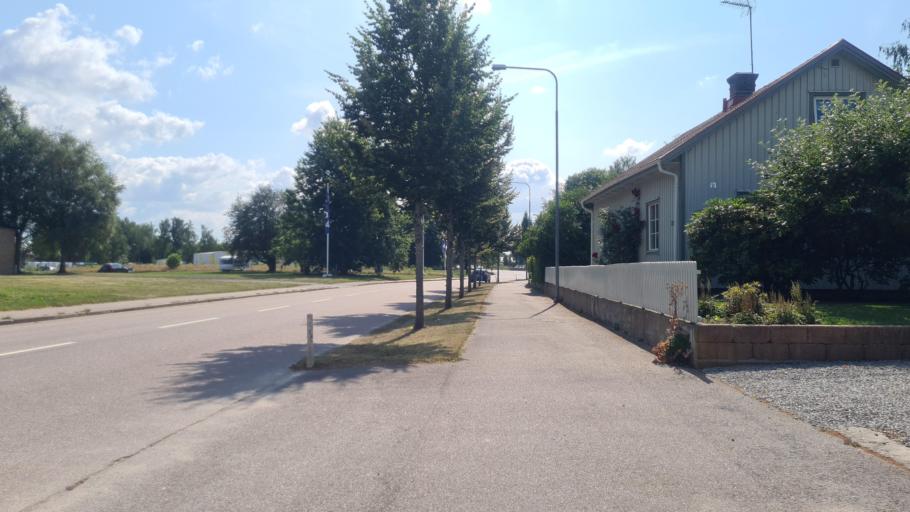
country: SE
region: Kronoberg
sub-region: Ljungby Kommun
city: Ljungby
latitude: 56.8291
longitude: 13.9273
